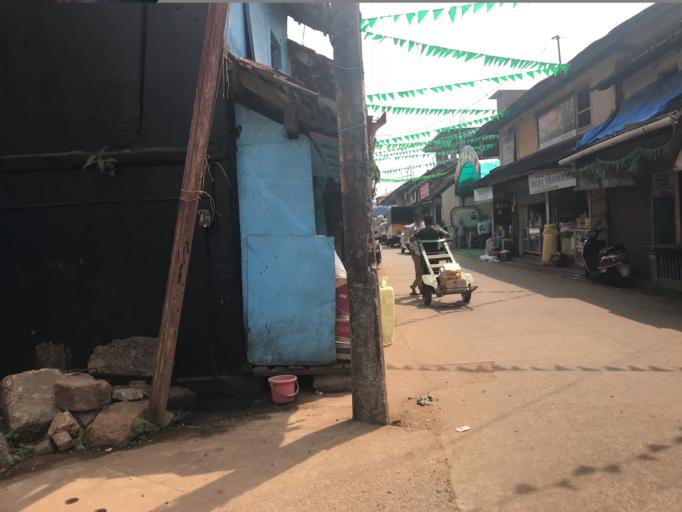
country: IN
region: Karnataka
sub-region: Dakshina Kannada
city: Mangalore
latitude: 12.8651
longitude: 74.8327
